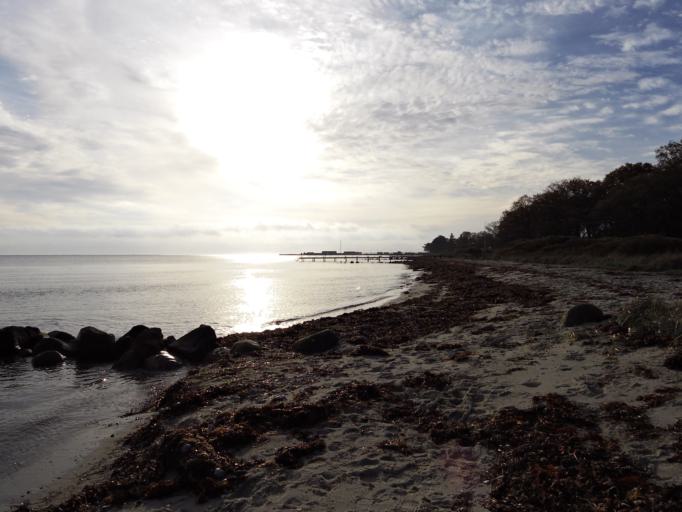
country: DK
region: Central Jutland
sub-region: Odder Kommune
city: Odder
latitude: 55.9205
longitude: 10.2567
